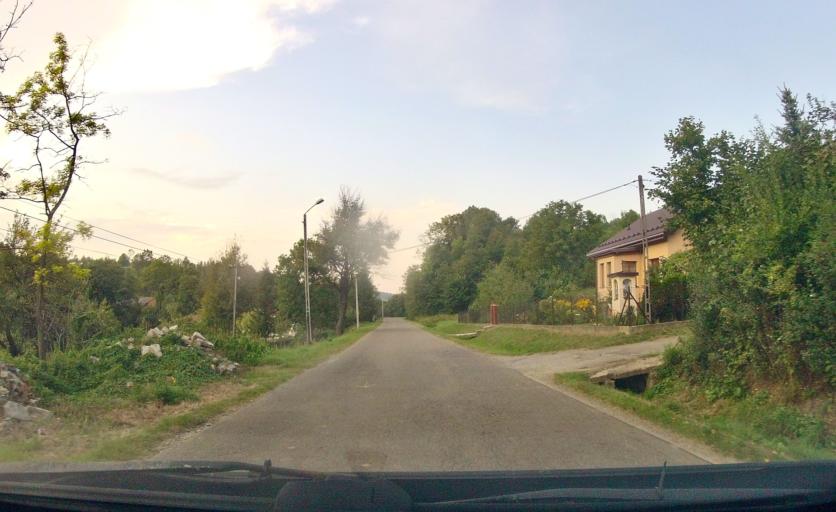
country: PL
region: Subcarpathian Voivodeship
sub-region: Powiat krosnienski
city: Dukla
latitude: 49.5491
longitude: 21.6227
